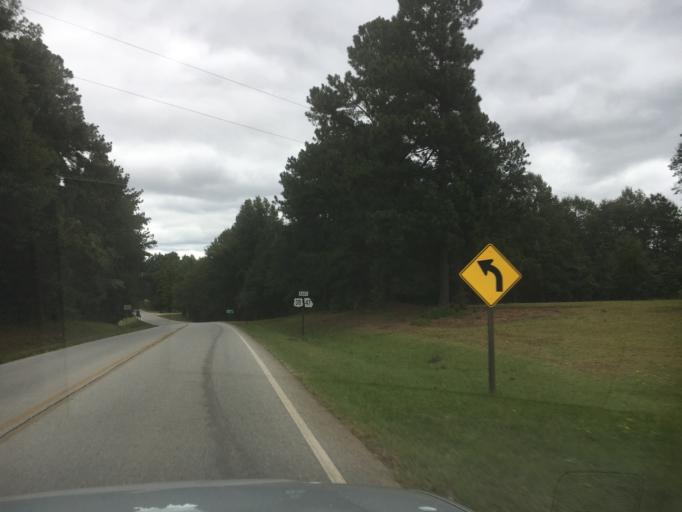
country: US
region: Georgia
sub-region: Lincoln County
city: Lincolnton
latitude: 33.7576
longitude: -82.5045
